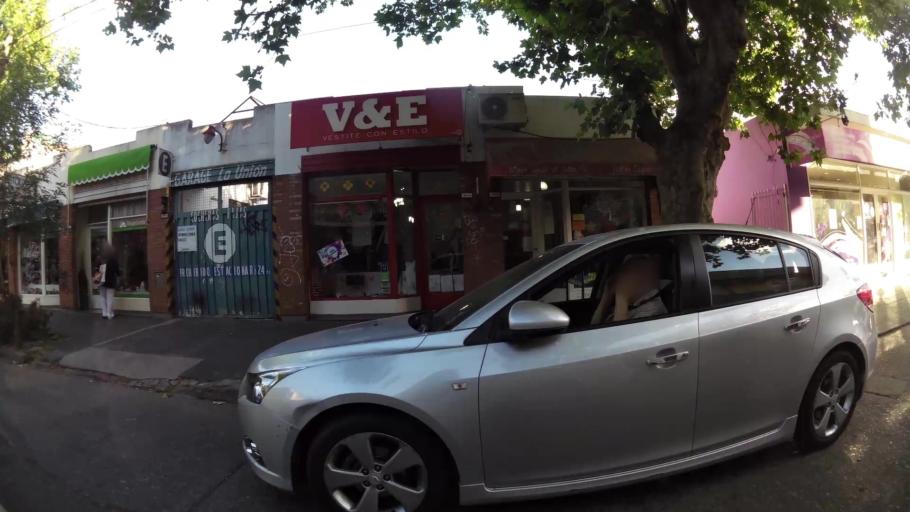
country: AR
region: Buenos Aires
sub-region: Partido de General San Martin
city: General San Martin
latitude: -34.5528
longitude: -58.5551
